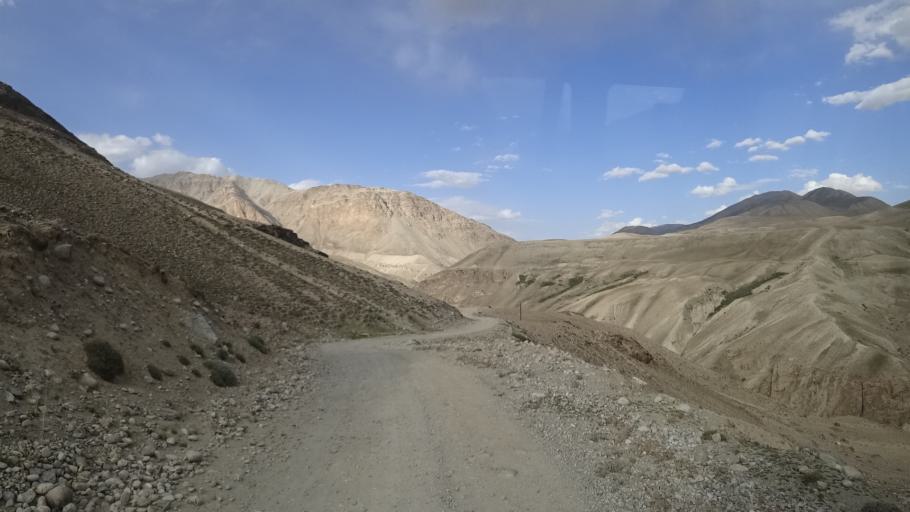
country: AF
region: Badakhshan
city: Khandud
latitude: 37.2240
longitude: 72.7987
